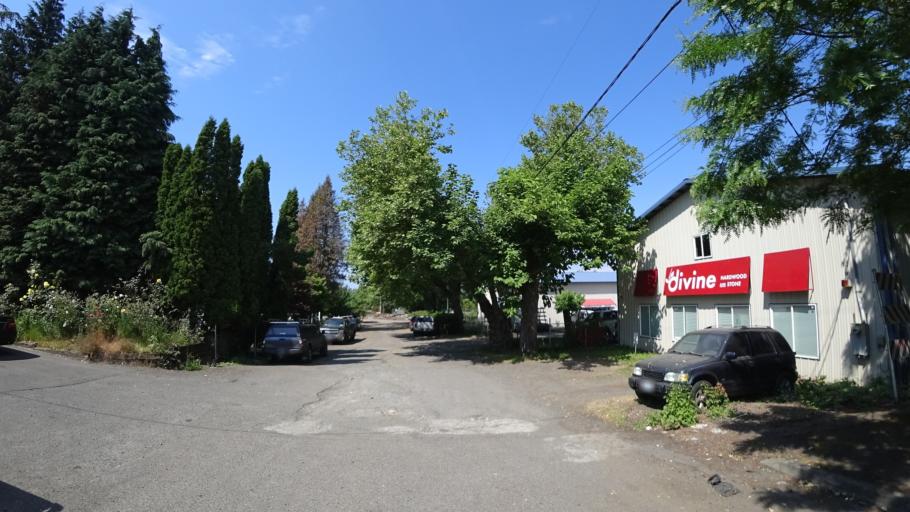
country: US
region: Oregon
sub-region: Multnomah County
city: Lents
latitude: 45.5589
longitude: -122.5506
